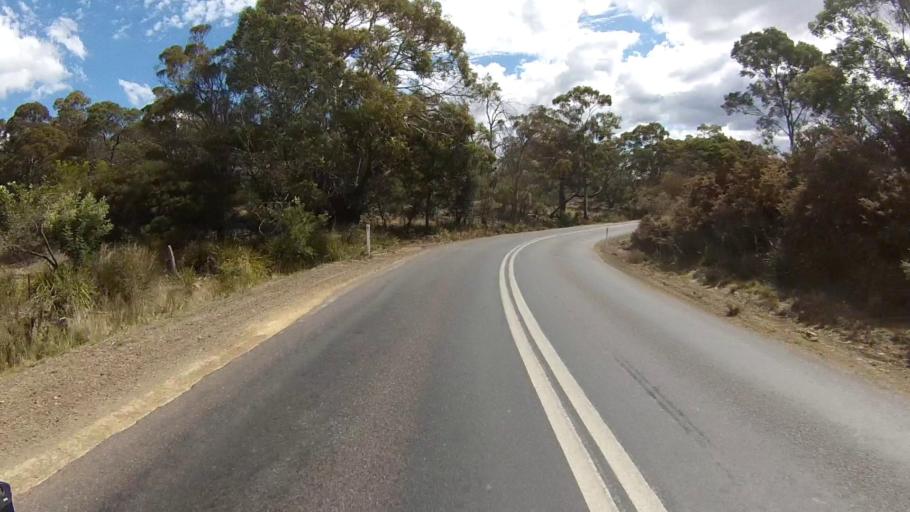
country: AU
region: Tasmania
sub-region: Break O'Day
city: St Helens
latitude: -41.9927
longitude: 148.1161
